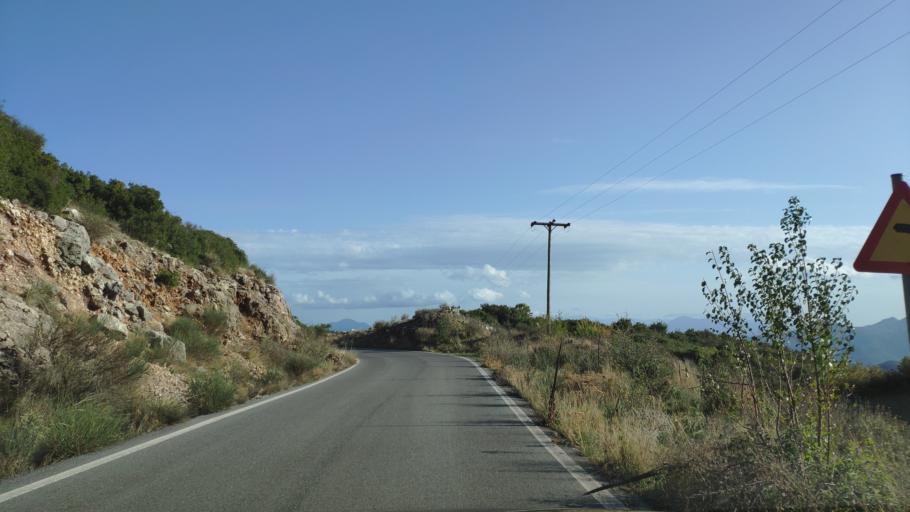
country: GR
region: Peloponnese
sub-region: Nomos Arkadias
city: Dimitsana
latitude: 37.5673
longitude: 22.0232
